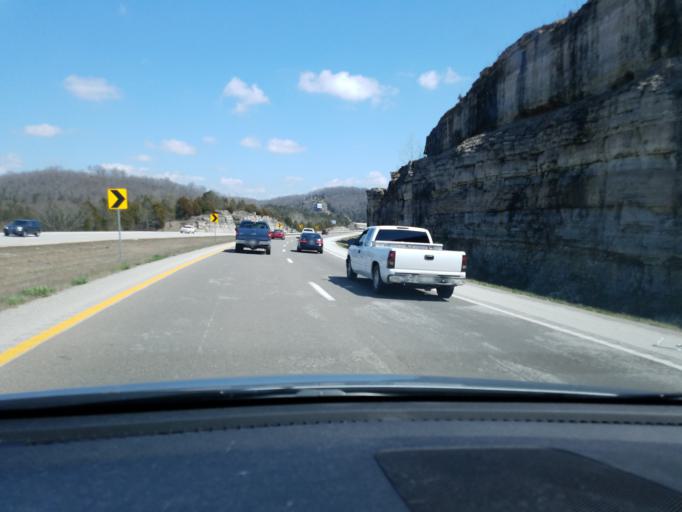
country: US
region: Missouri
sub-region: Taney County
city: Merriam Woods
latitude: 36.8226
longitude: -93.2261
